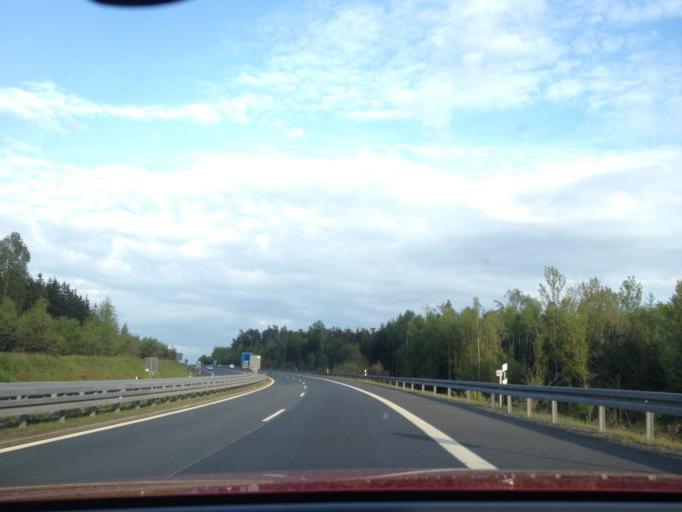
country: DE
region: Bavaria
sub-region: Upper Palatinate
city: Pechbrunn
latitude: 49.9540
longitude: 12.1958
